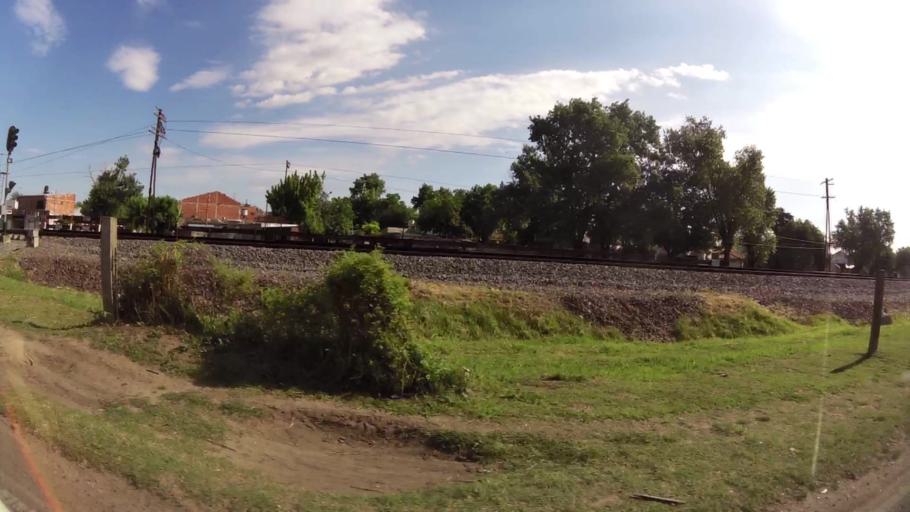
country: AR
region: Buenos Aires
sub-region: Partido de Merlo
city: Merlo
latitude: -34.6627
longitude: -58.7394
